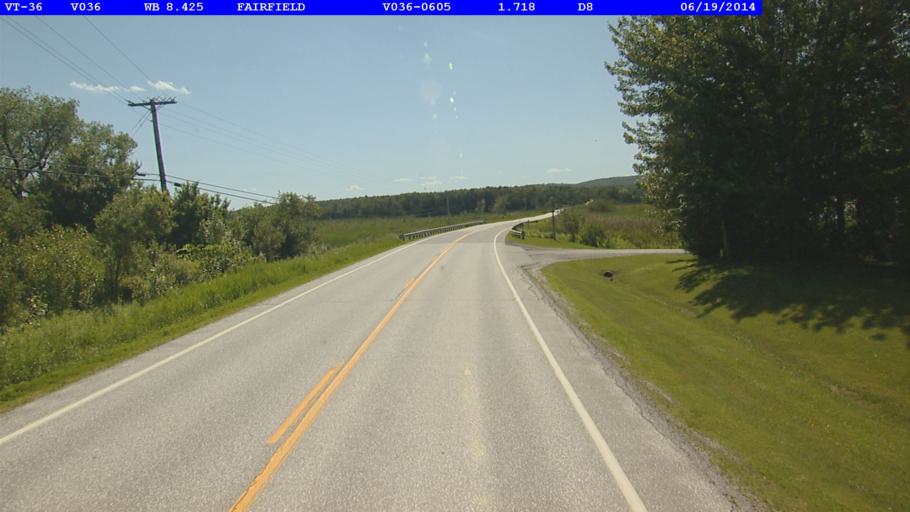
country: US
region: Vermont
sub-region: Franklin County
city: Saint Albans
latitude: 44.7877
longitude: -72.9974
